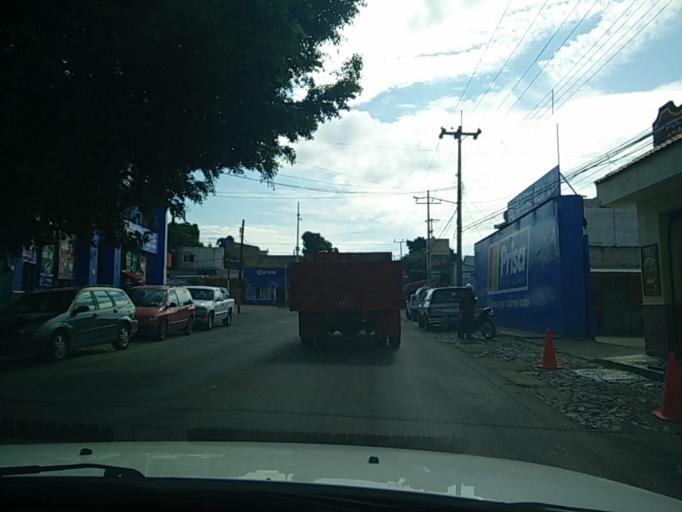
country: MX
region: Jalisco
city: Ajijic
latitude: 20.3011
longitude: -103.2608
